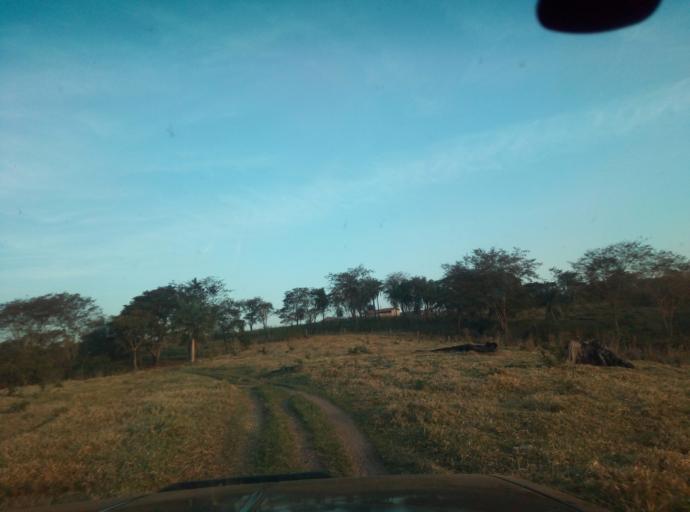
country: PY
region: Caaguazu
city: Yhu
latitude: -25.2048
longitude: -56.1066
